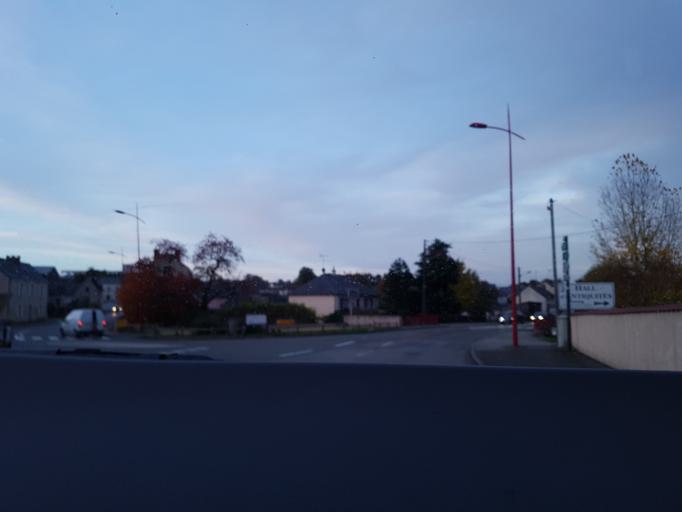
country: FR
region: Pays de la Loire
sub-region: Departement de la Mayenne
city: Cosse-le-Vivien
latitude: 47.9480
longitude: -0.9098
